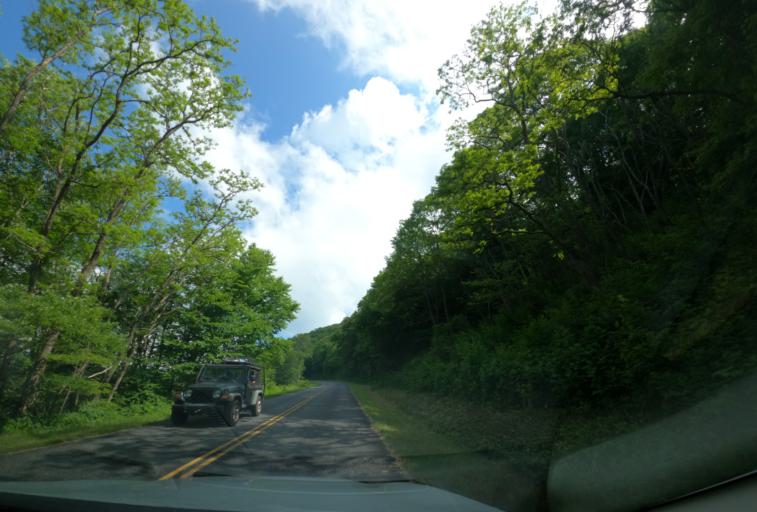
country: US
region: North Carolina
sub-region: Haywood County
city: Hazelwood
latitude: 35.4035
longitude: -83.0451
